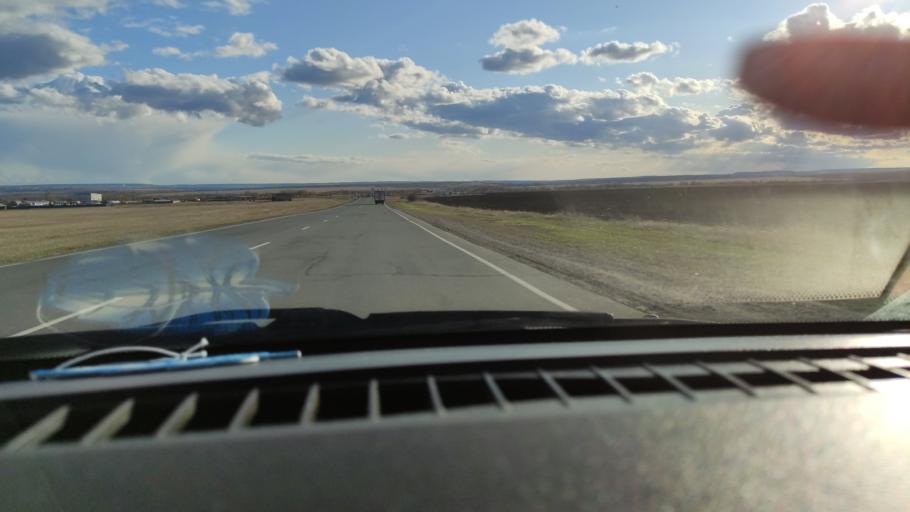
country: RU
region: Saratov
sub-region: Saratovskiy Rayon
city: Saratov
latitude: 51.7370
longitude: 46.0388
